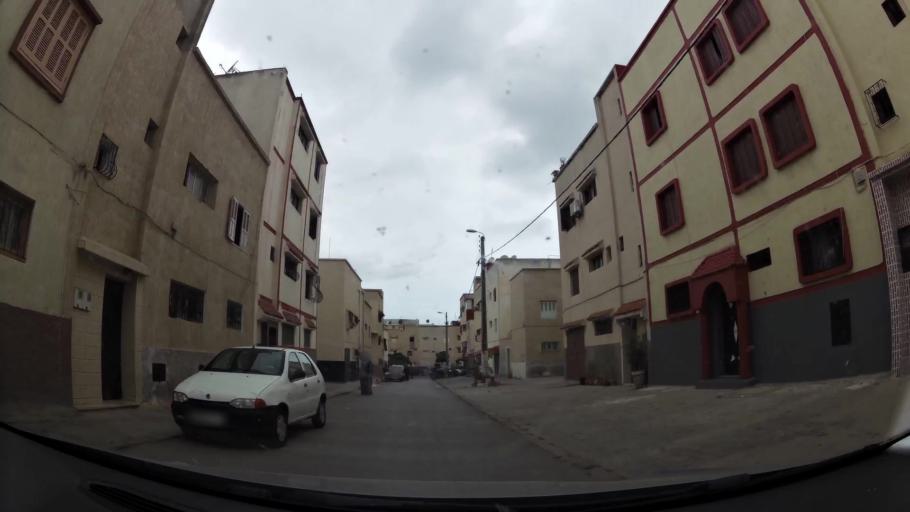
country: MA
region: Rabat-Sale-Zemmour-Zaer
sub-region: Rabat
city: Rabat
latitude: 33.9954
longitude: -6.8160
